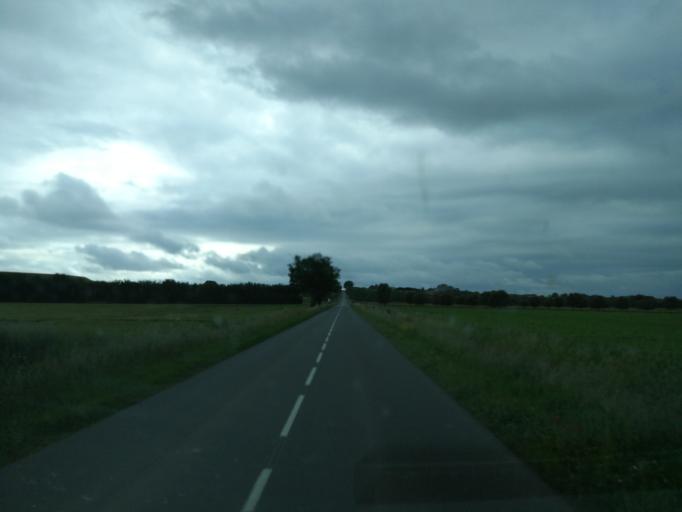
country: FR
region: Pays de la Loire
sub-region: Departement de la Vendee
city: Vix
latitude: 46.3718
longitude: -0.8953
